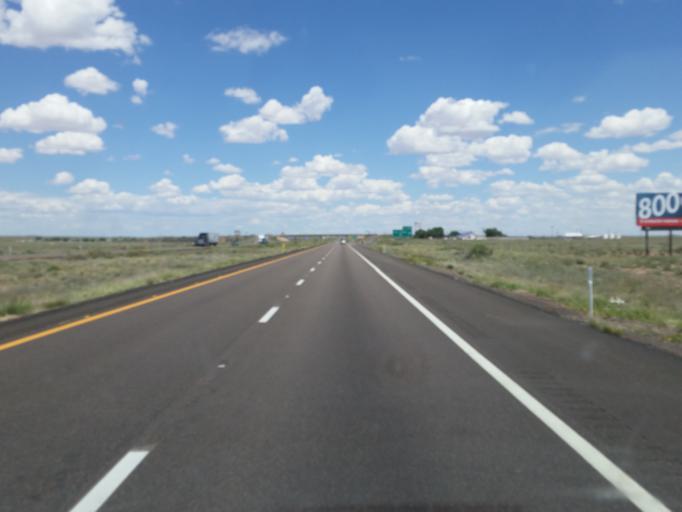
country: US
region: Arizona
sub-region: Navajo County
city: Holbrook
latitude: 34.9786
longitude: -110.0655
